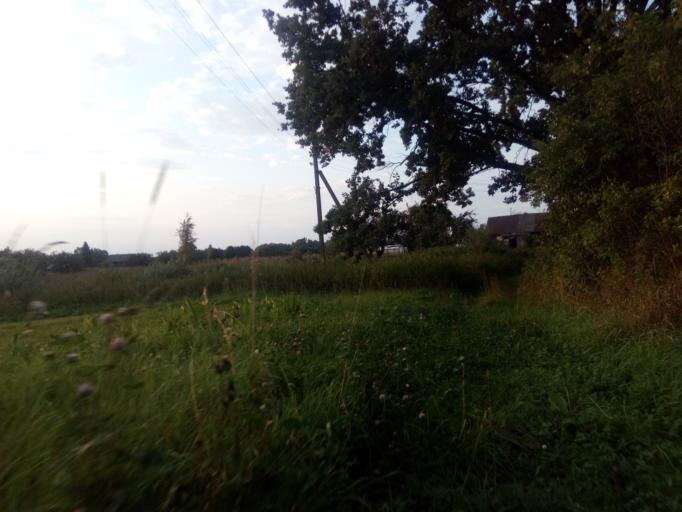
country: BY
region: Vitebsk
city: Dzisna
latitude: 55.6617
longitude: 28.3323
